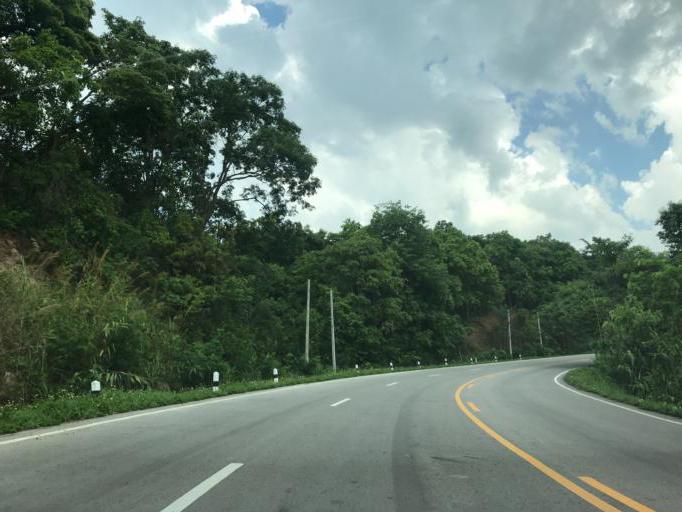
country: TH
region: Phayao
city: Phayao
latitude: 19.0791
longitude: 99.8146
